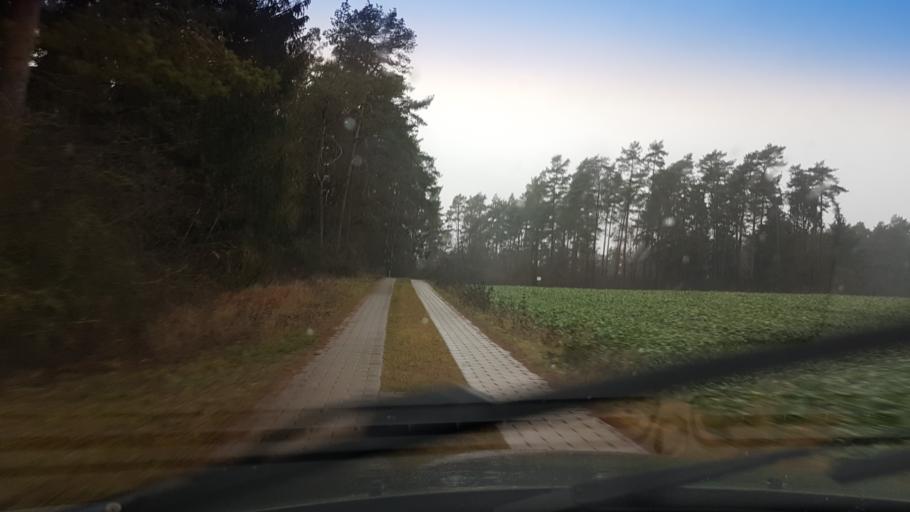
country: DE
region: Bavaria
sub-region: Upper Franconia
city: Kasendorf
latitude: 50.0379
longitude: 11.3040
